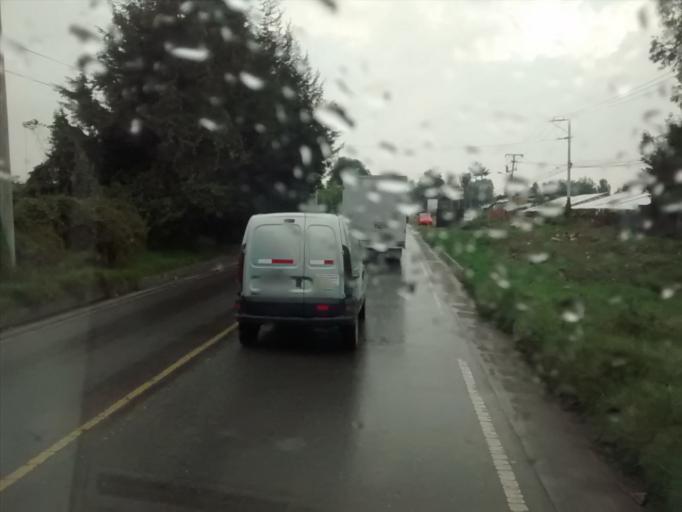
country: CO
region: Cundinamarca
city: Cota
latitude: 4.7640
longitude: -74.0895
